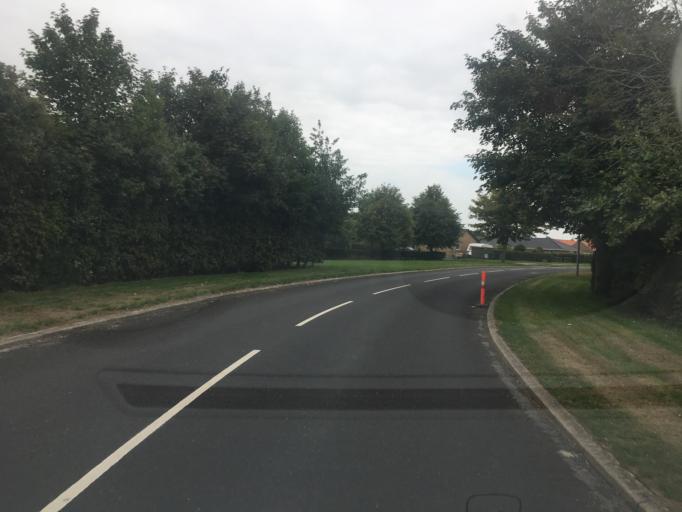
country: DK
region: South Denmark
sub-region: Tonder Kommune
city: Tonder
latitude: 54.9340
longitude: 8.8512
